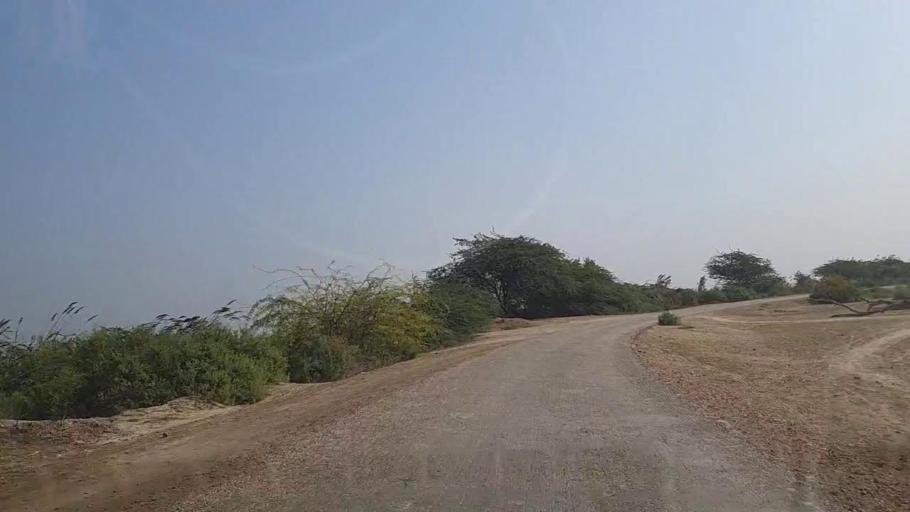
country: PK
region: Sindh
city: Keti Bandar
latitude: 24.2289
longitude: 67.6640
